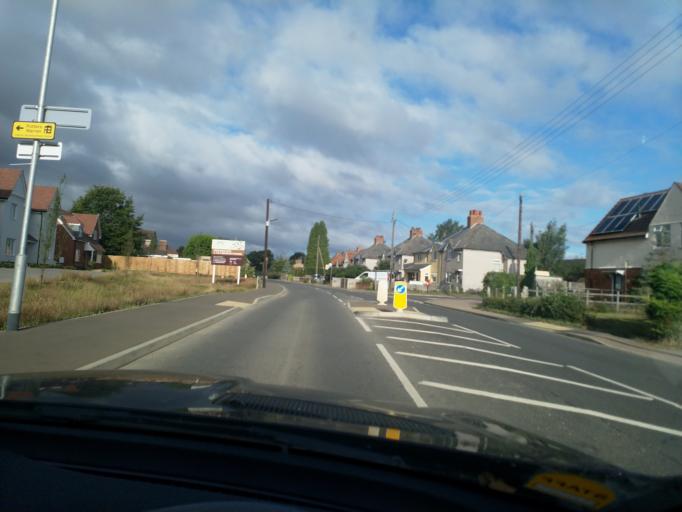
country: GB
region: England
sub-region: Suffolk
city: Elmswell
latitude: 52.2318
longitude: 0.9188
